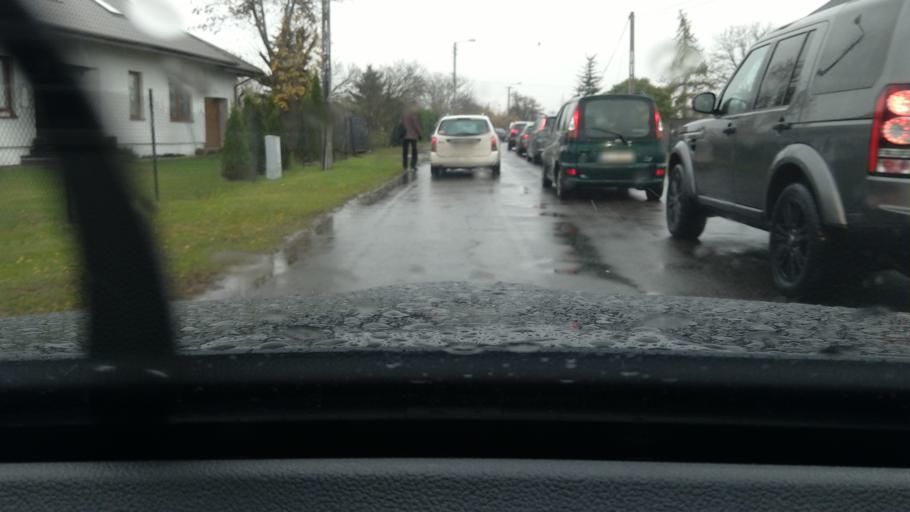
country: PL
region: Lodz Voivodeship
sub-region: Skierniewice
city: Skierniewice
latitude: 51.9434
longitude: 20.1523
